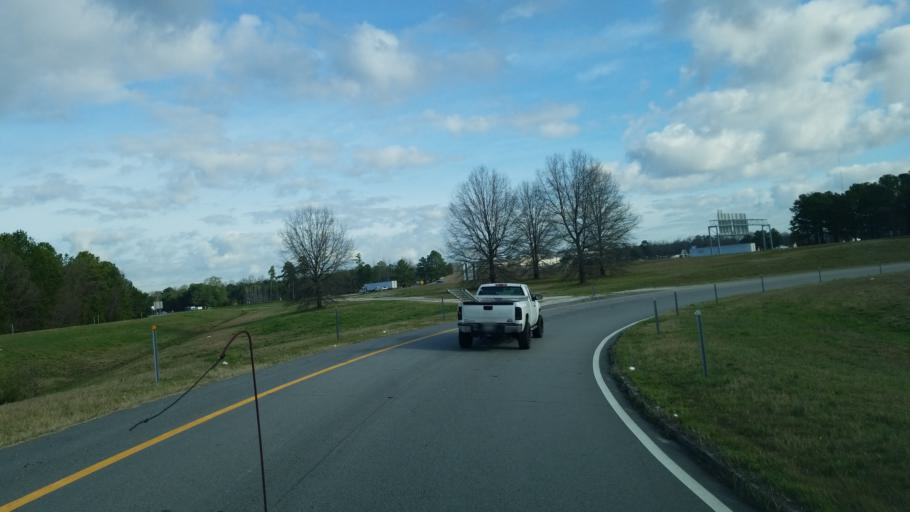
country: US
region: South Carolina
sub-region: Richland County
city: Dentsville
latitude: 34.1004
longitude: -80.9606
